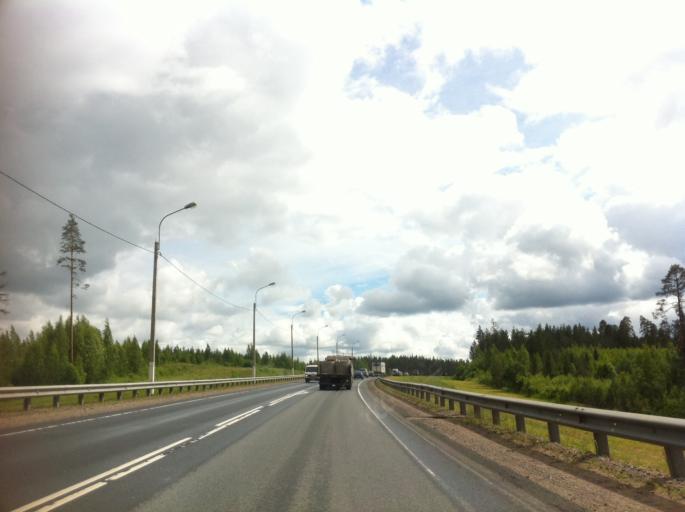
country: RU
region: Leningrad
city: Luga
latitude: 58.7516
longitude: 29.8931
